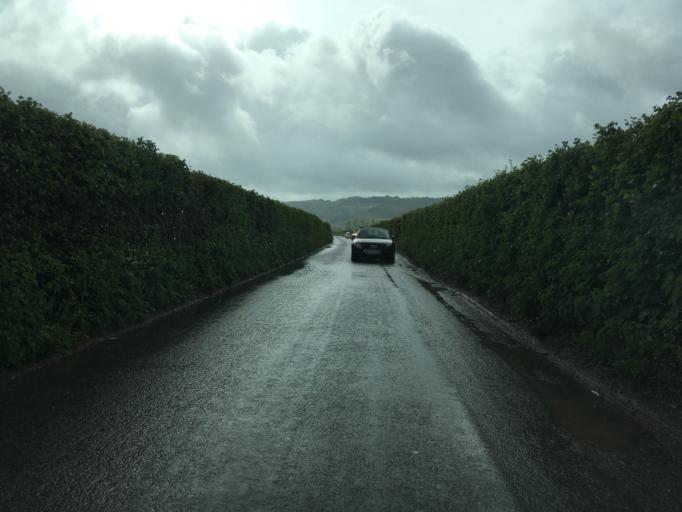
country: GB
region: England
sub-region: North Somerset
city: Burrington
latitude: 51.3440
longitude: -2.7499
